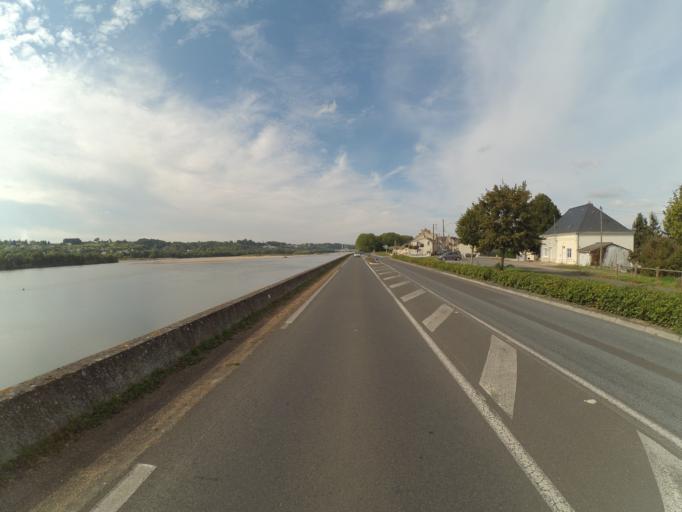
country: FR
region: Pays de la Loire
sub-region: Departement de Maine-et-Loire
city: Villebernier
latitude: 47.2515
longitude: -0.0278
